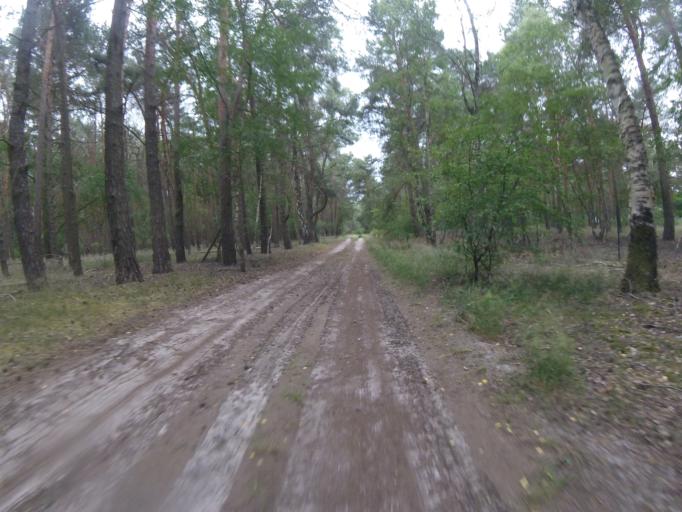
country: DE
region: Brandenburg
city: Bestensee
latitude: 52.2160
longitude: 13.6167
